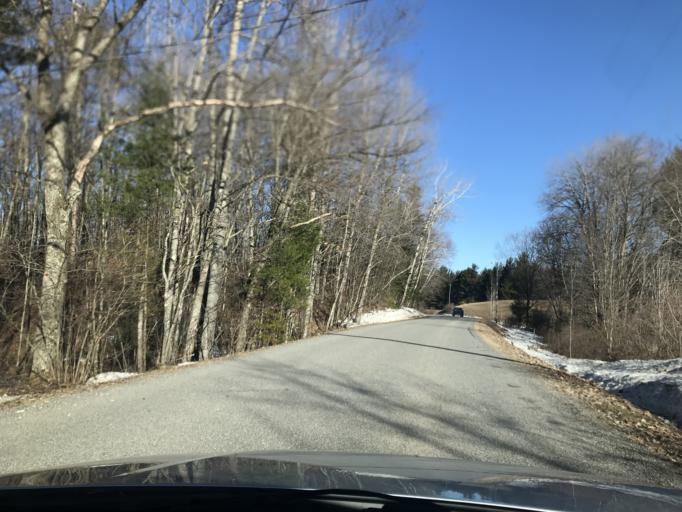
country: US
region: Wisconsin
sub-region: Marinette County
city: Niagara
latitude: 45.3872
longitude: -88.0453
